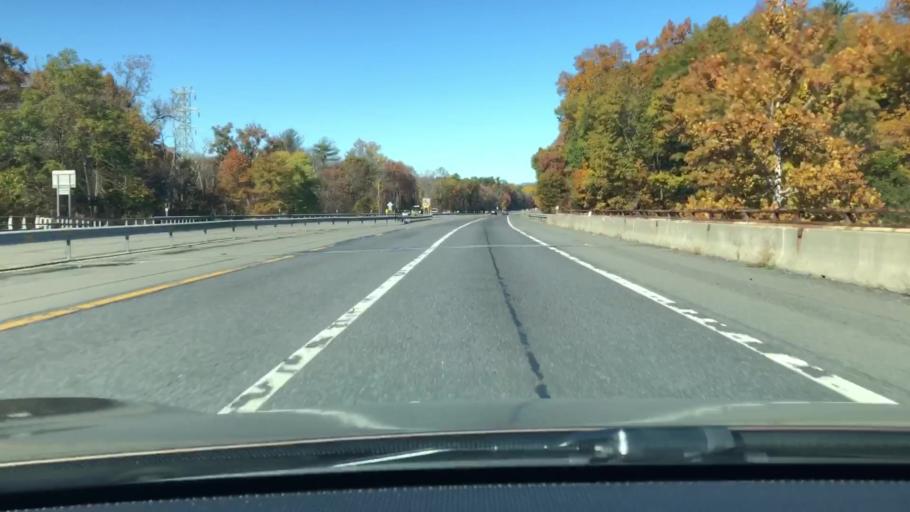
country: US
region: New York
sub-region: Ulster County
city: Tillson
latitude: 41.8176
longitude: -74.0562
